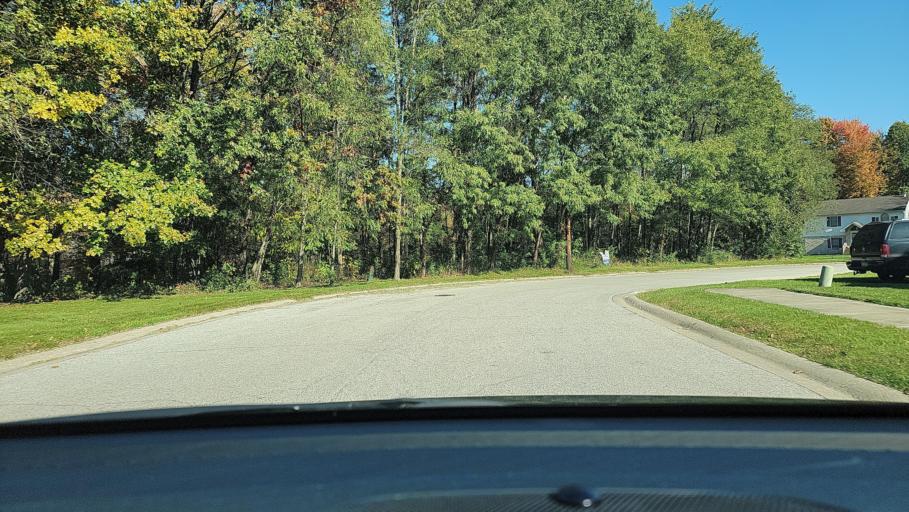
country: US
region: Indiana
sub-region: Porter County
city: Portage
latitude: 41.5794
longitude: -87.1581
